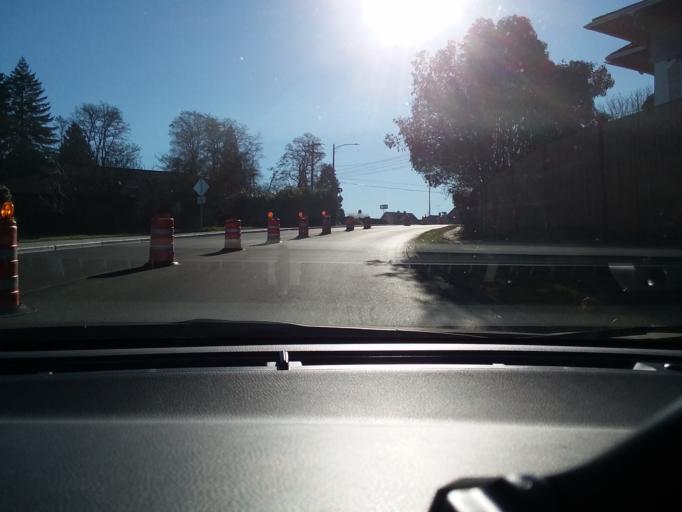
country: US
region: Washington
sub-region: Pierce County
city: Tacoma
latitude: 47.2332
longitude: -122.4226
